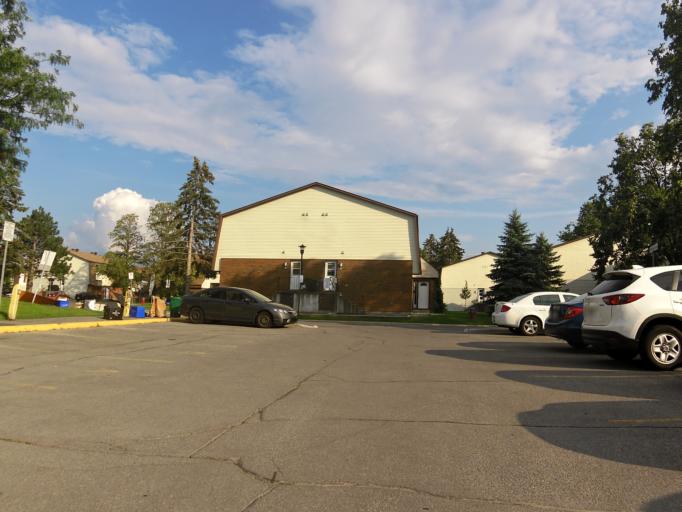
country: CA
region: Ontario
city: Bells Corners
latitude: 45.3330
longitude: -75.7602
